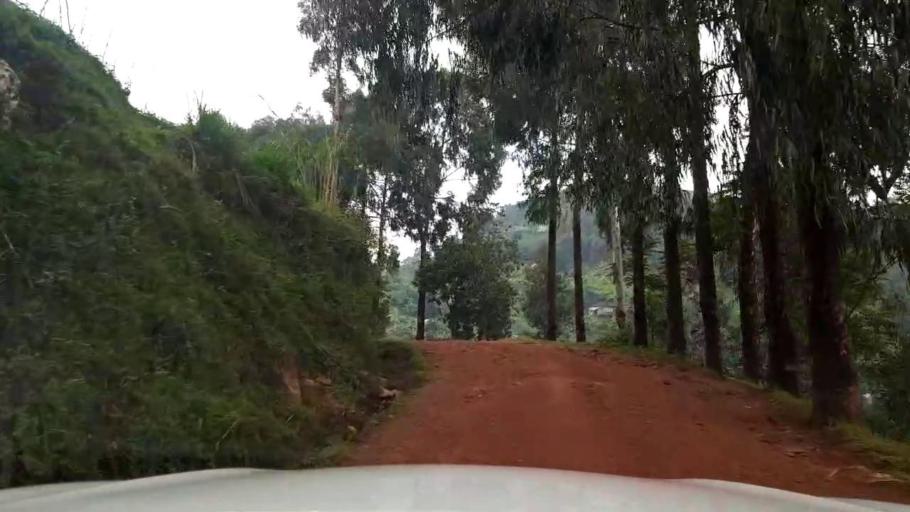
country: UG
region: Western Region
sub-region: Kisoro District
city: Kisoro
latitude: -1.4032
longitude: 29.8010
